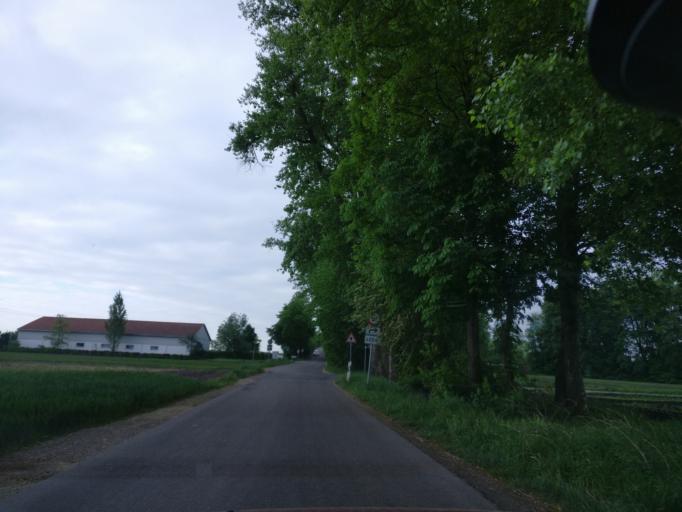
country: DE
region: Bavaria
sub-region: Upper Bavaria
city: Karlsfeld
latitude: 48.2077
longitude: 11.4320
